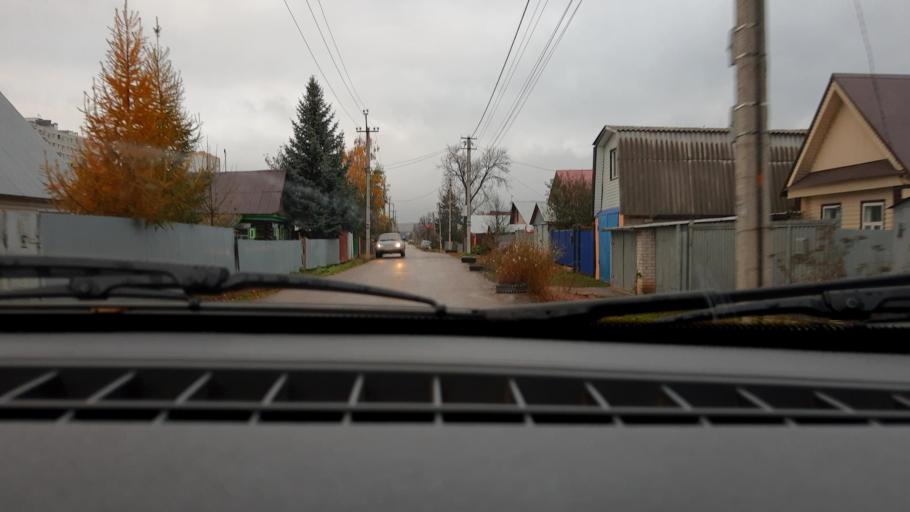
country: RU
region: Bashkortostan
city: Mikhaylovka
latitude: 54.7877
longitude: 55.8890
